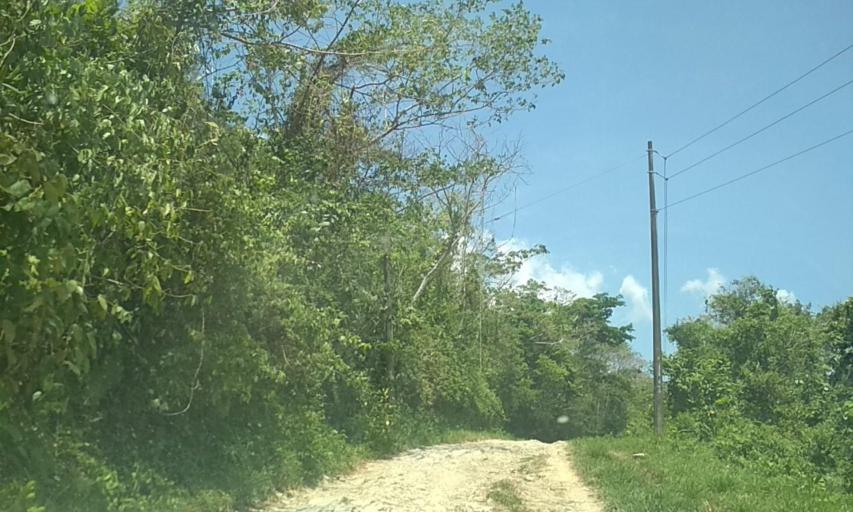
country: MX
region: Chiapas
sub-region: Tecpatan
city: Raudales Malpaso
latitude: 17.3020
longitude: -93.8258
